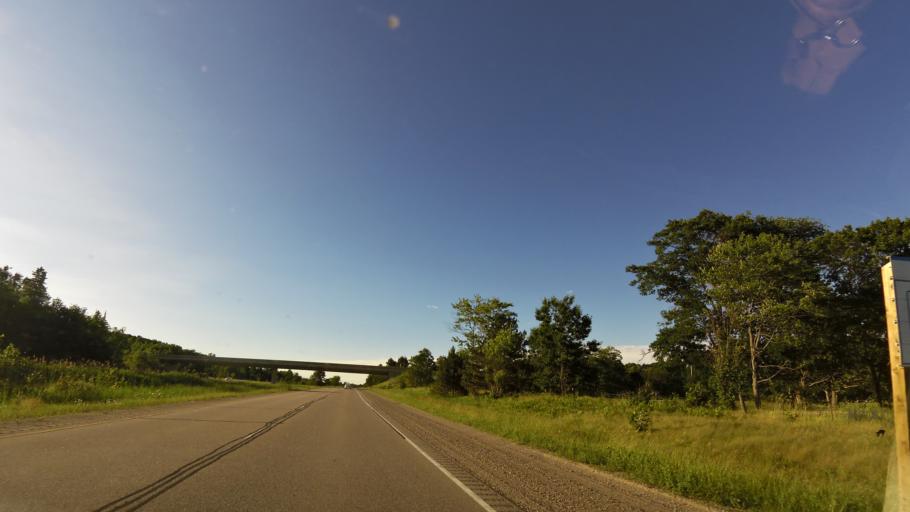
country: CA
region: Ontario
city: Orillia
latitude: 44.6836
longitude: -79.6469
